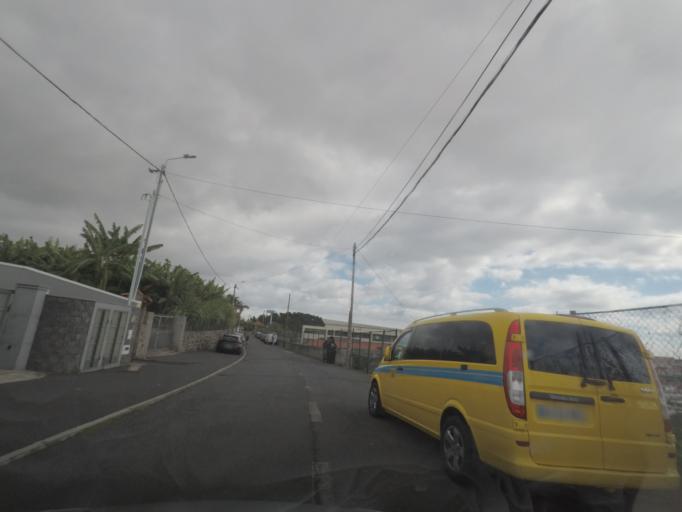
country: PT
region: Madeira
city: Camara de Lobos
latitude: 32.6542
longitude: -16.9459
